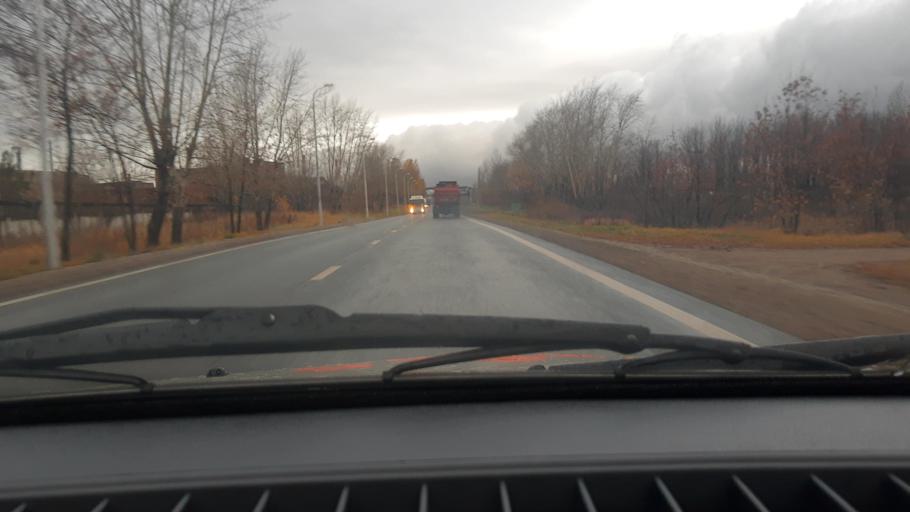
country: RU
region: Bashkortostan
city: Ufa
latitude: 54.8415
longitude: 56.1231
